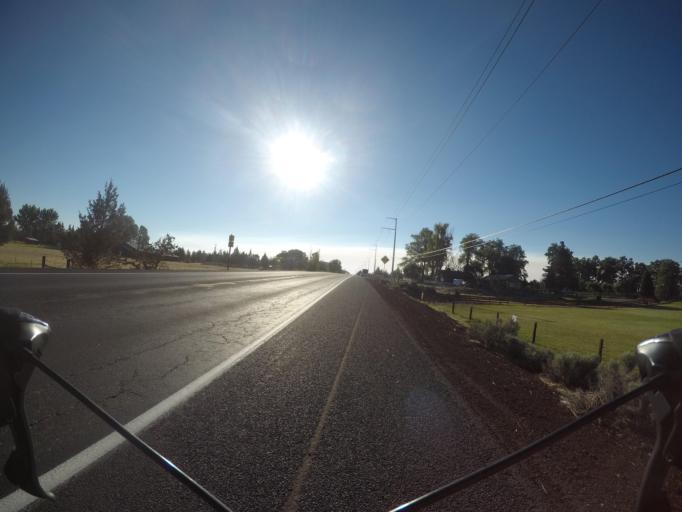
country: US
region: Oregon
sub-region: Deschutes County
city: Redmond
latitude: 44.2730
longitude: -121.2527
